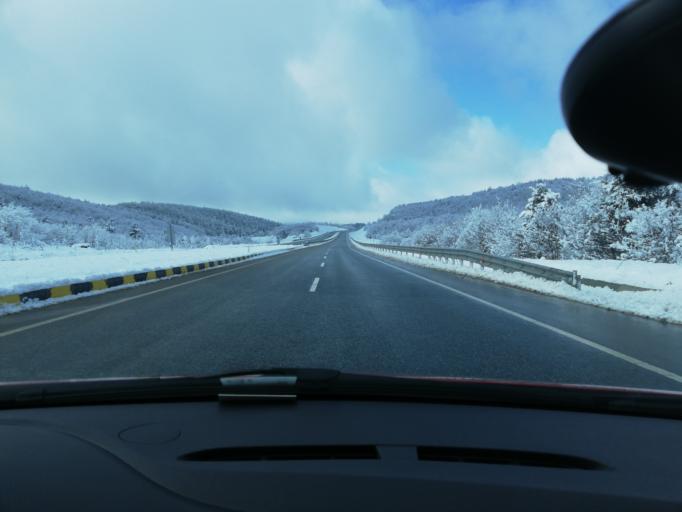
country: TR
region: Kastamonu
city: Ihsangazi
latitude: 41.3301
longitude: 33.6190
